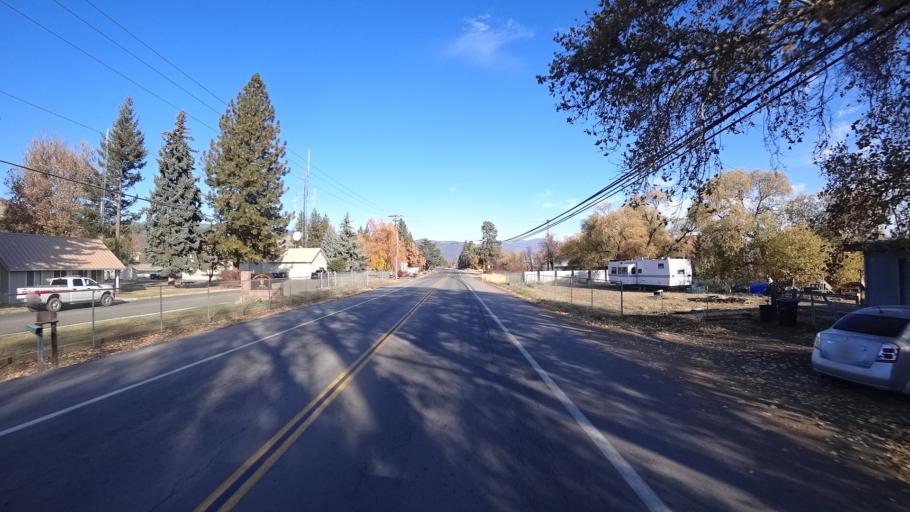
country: US
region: California
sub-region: Siskiyou County
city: Yreka
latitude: 41.7016
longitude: -122.6404
